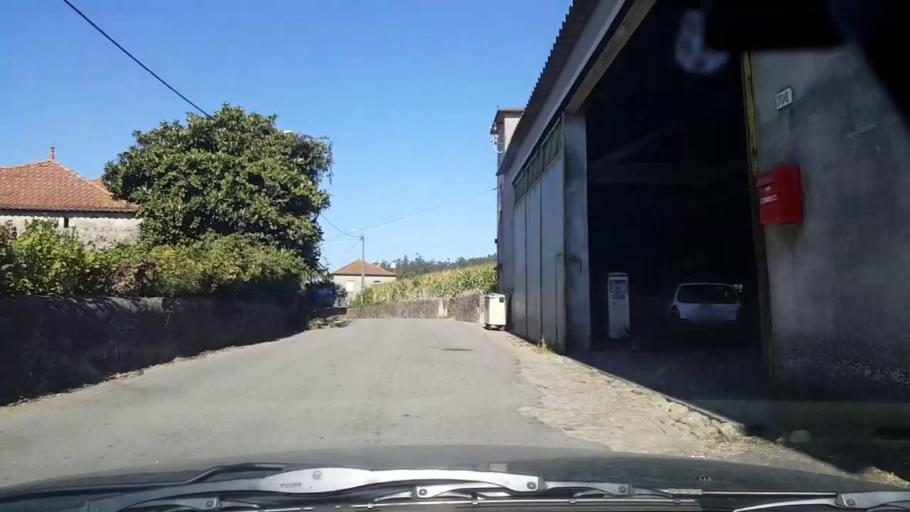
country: PT
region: Braga
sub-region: Vila Nova de Famalicao
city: Ribeirao
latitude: 41.3719
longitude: -8.6445
